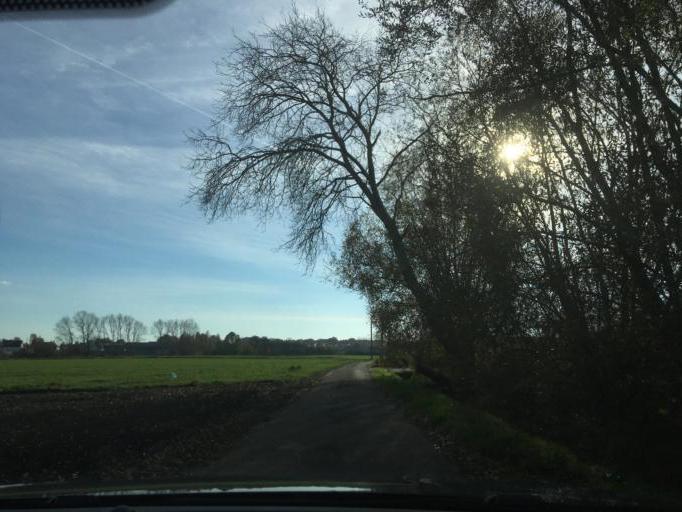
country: BE
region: Flanders
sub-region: Provincie West-Vlaanderen
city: Pittem
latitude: 50.9739
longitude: 3.2404
